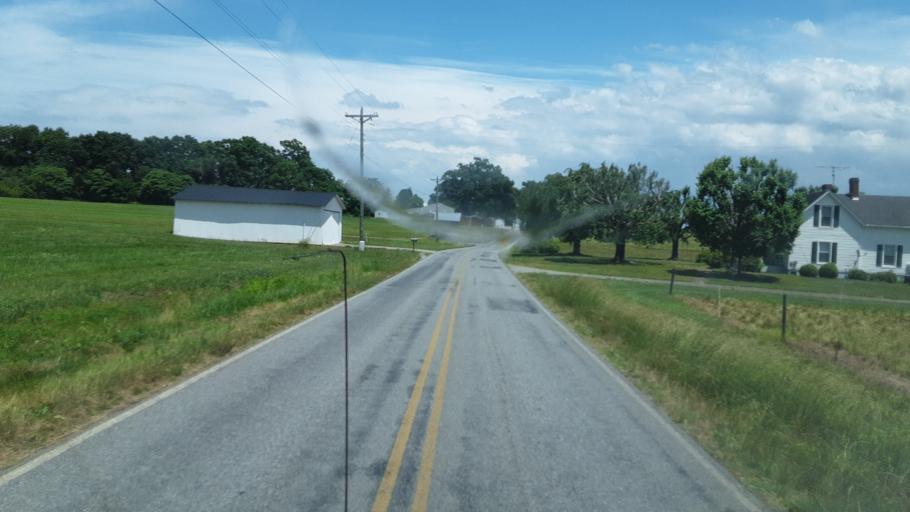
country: US
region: North Carolina
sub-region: Yadkin County
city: Yadkinville
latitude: 36.0682
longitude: -80.8177
